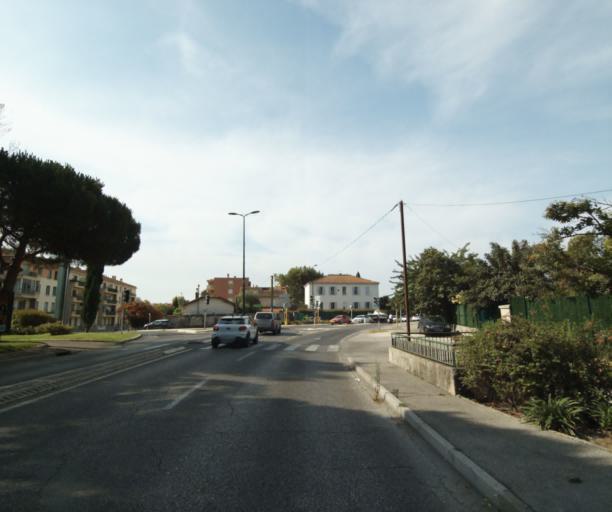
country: FR
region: Provence-Alpes-Cote d'Azur
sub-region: Departement du Var
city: La Garde
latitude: 43.1239
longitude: 6.0042
